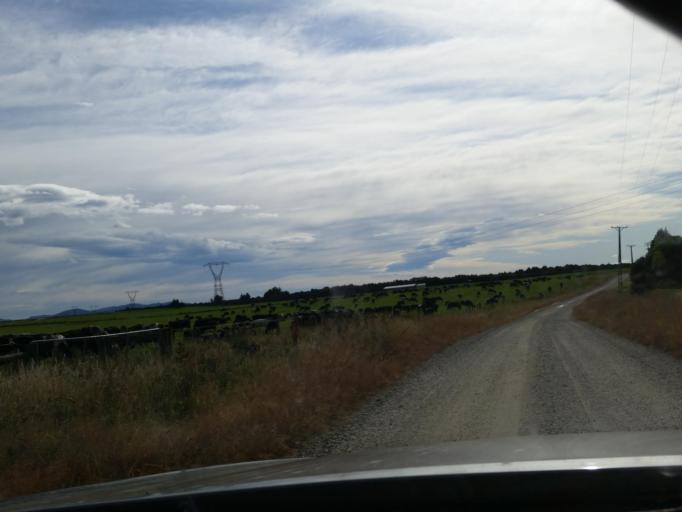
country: NZ
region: Southland
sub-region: Invercargill City
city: Invercargill
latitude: -46.2747
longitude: 168.5014
